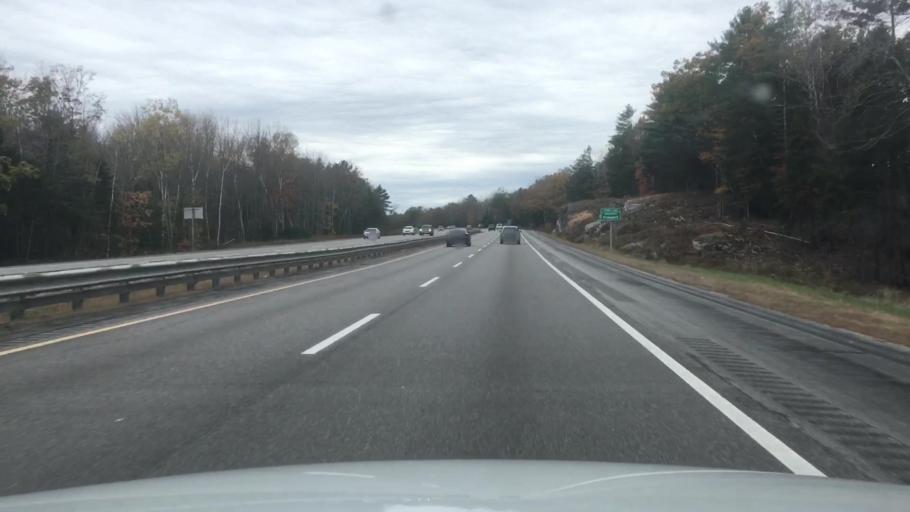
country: US
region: Maine
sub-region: Cumberland County
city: Freeport
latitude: 43.9029
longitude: -70.0685
